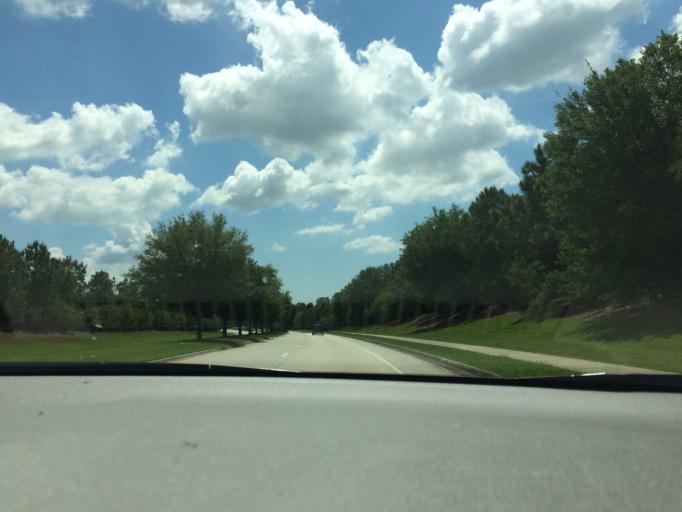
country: US
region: Florida
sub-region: Sarasota County
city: The Meadows
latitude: 27.4220
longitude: -82.3985
